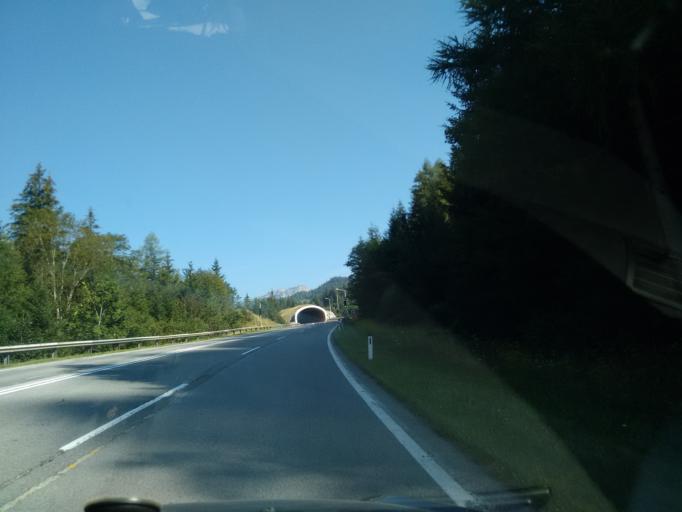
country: AT
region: Styria
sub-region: Politischer Bezirk Liezen
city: Irdning
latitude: 47.5275
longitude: 14.0591
